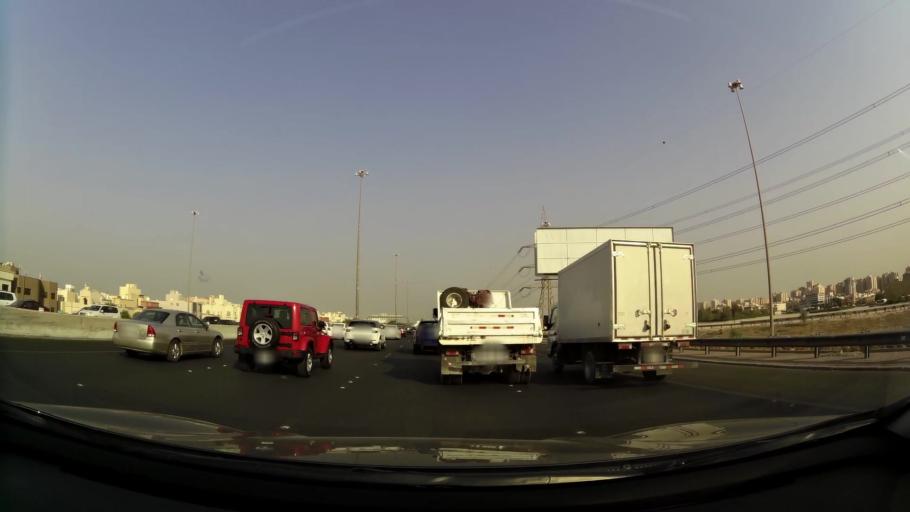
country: KW
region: Al Farwaniyah
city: Al Farwaniyah
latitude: 29.3029
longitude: 47.9653
